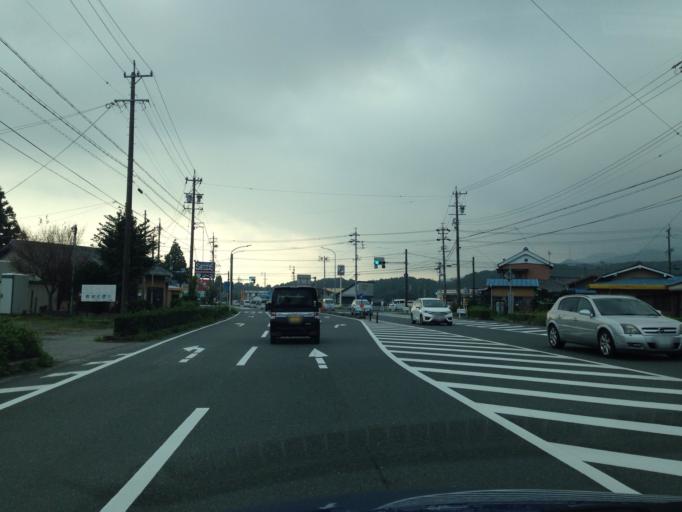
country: JP
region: Aichi
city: Shinshiro
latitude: 34.9011
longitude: 137.4839
